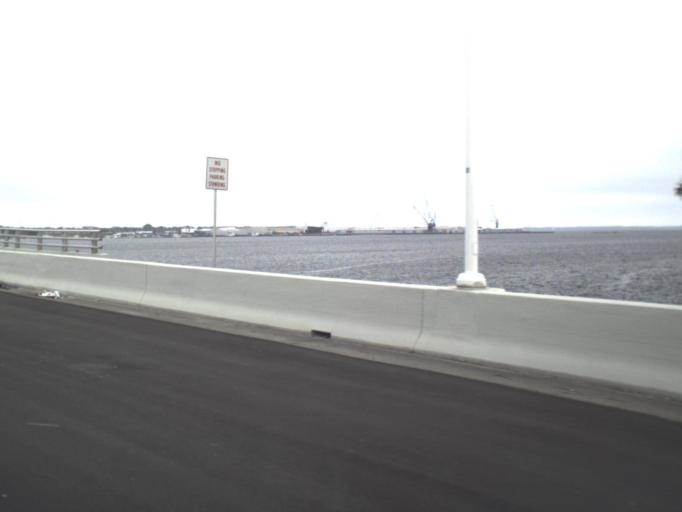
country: US
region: Florida
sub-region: Bay County
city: Upper Grand Lagoon
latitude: 30.1880
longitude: -85.7481
